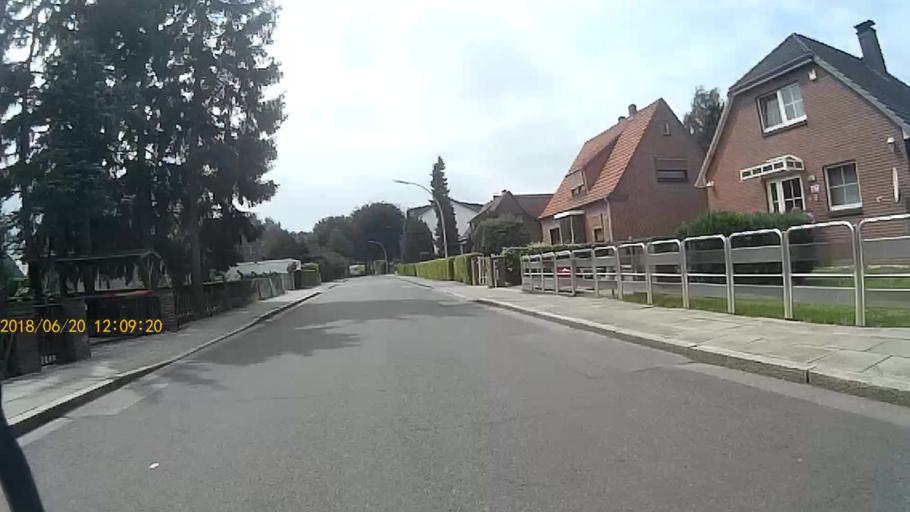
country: DE
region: Hamburg
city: Harburg
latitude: 53.4820
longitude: 10.0076
